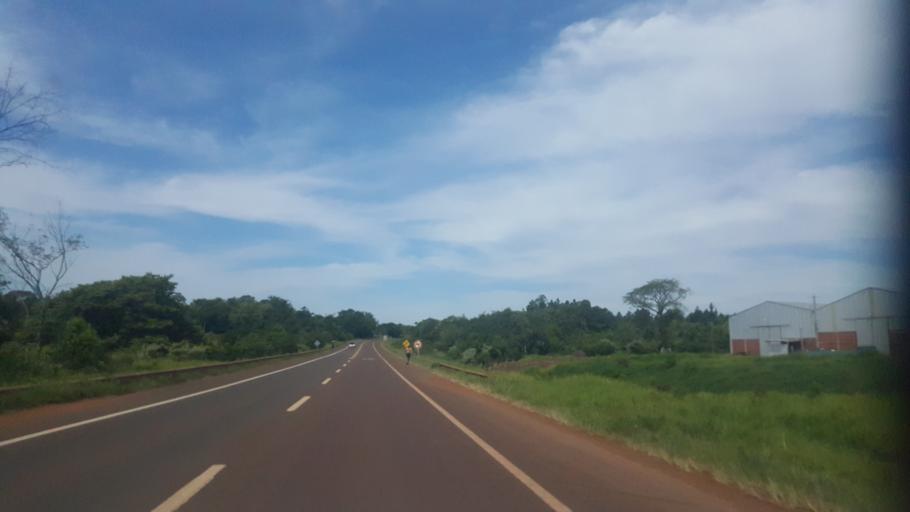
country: AR
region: Misiones
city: Cerro Azul
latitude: -27.6372
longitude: -55.4898
